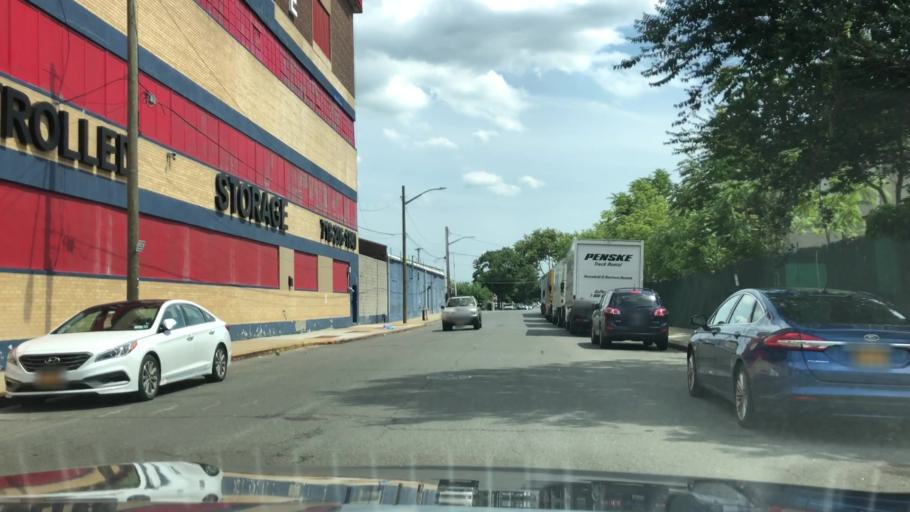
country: US
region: New York
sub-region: Queens County
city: Jamaica
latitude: 40.7007
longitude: -73.7749
